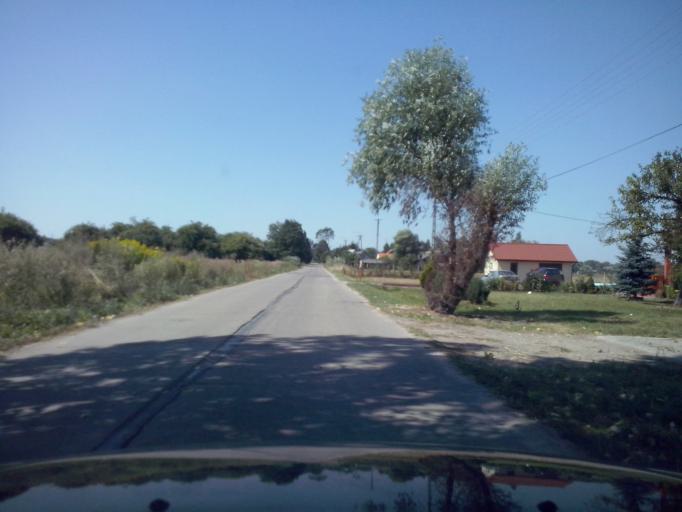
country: PL
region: Swietokrzyskie
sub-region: Powiat buski
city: Gnojno
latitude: 50.5965
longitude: 20.8128
